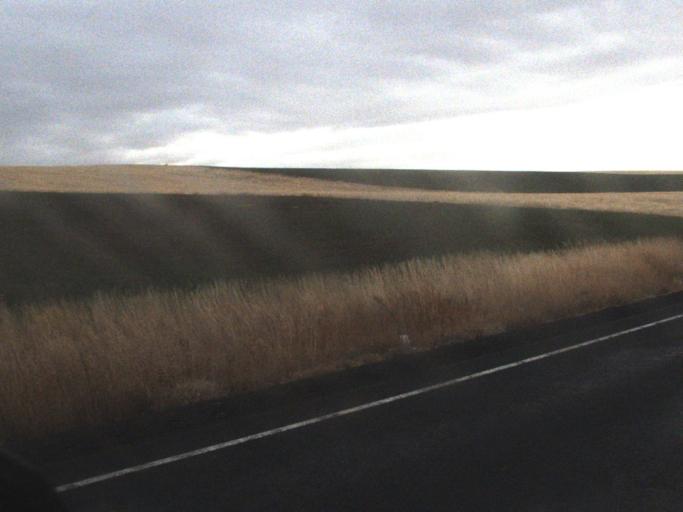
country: US
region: Washington
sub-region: Lincoln County
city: Davenport
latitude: 47.7168
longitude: -118.1515
